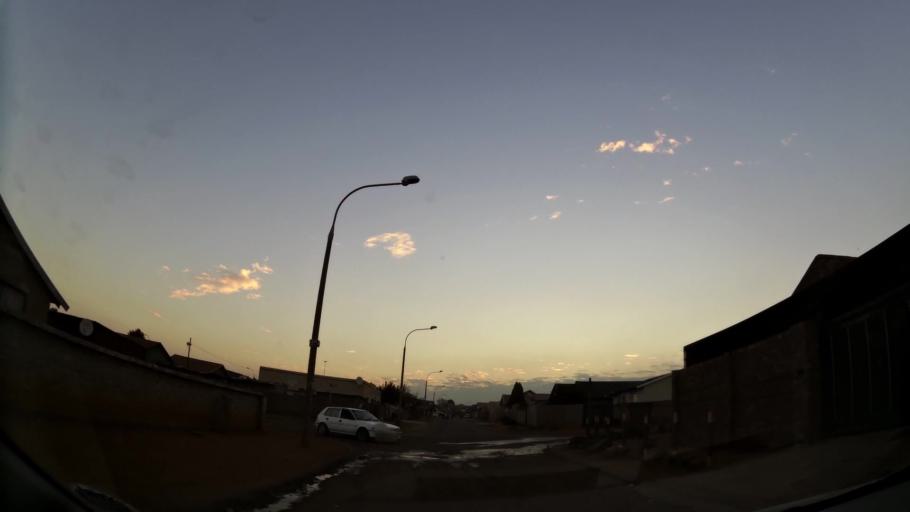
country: ZA
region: Gauteng
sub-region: West Rand District Municipality
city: Randfontein
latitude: -26.2112
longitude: 27.7170
